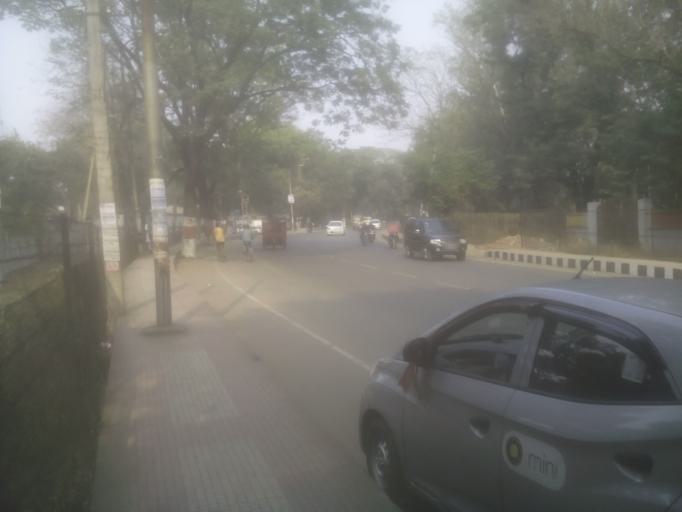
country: IN
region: Jharkhand
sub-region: Dhanbad
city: Dhanbad
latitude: 23.8027
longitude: 86.4271
